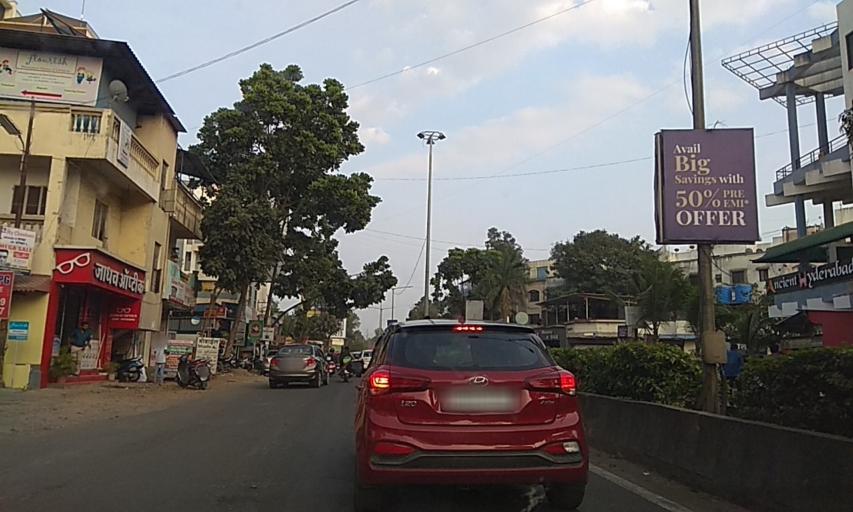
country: IN
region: Maharashtra
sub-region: Pune Division
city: Pimpri
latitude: 18.5884
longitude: 73.7832
